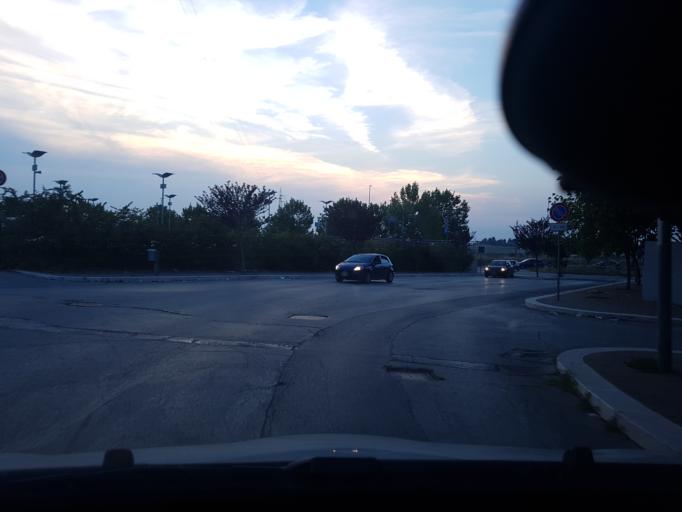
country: IT
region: Apulia
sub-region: Provincia di Foggia
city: Cerignola
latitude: 41.2633
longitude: 15.8795
